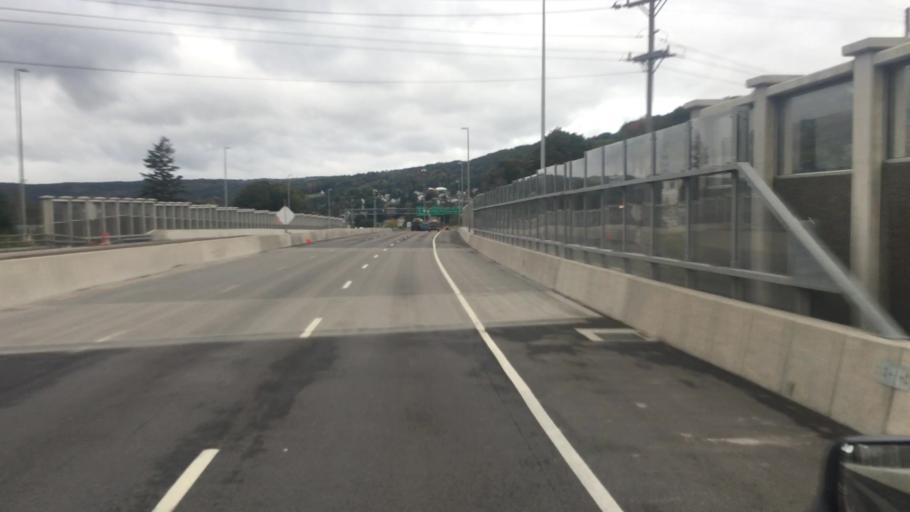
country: US
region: New York
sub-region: Broome County
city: Johnson City
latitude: 42.1172
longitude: -75.9402
